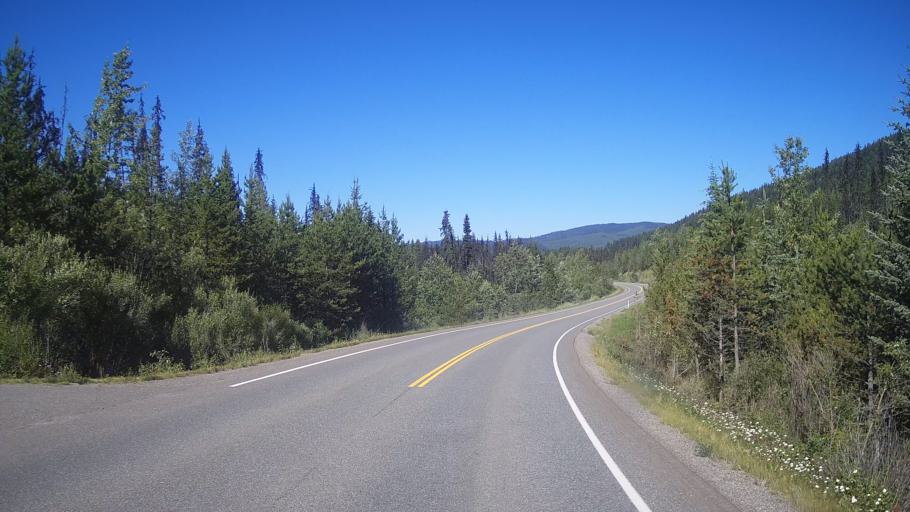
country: CA
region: British Columbia
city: Kamloops
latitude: 51.4950
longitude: -120.4086
